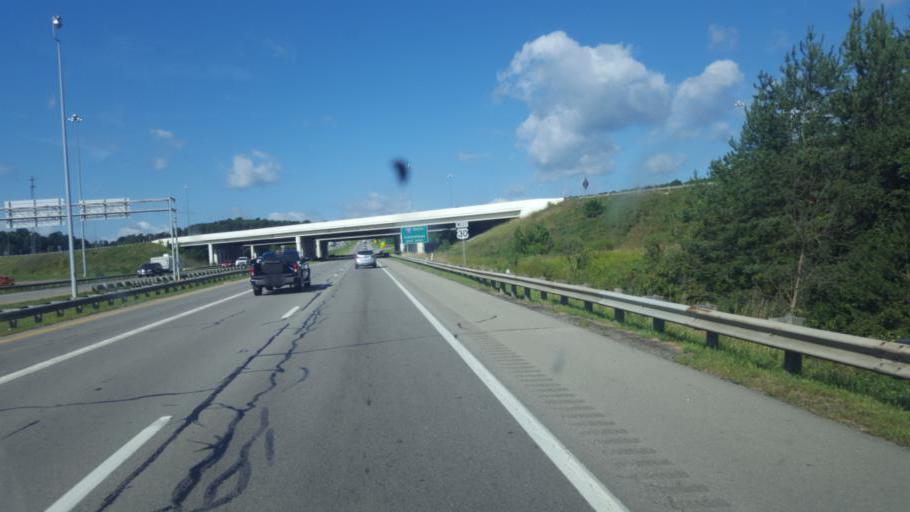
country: US
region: Ohio
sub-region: Richland County
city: Lincoln Heights
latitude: 40.7832
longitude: -82.4103
